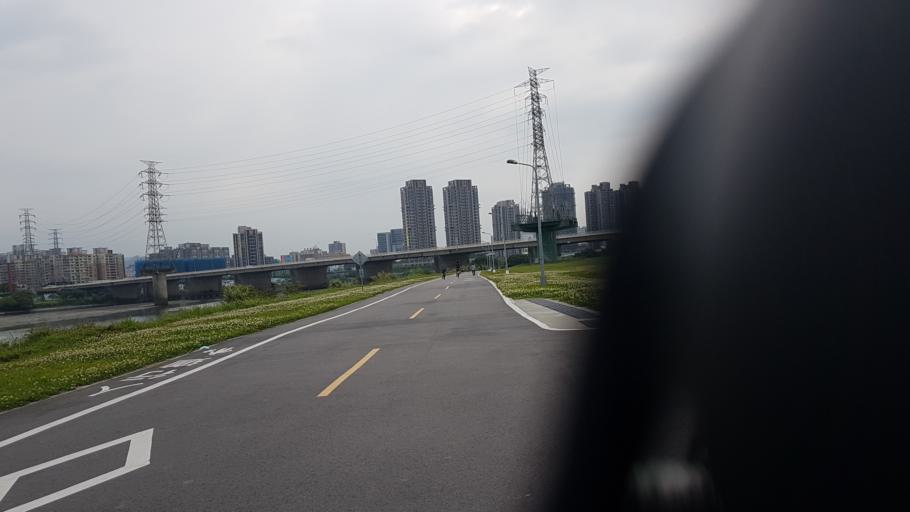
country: TW
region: Taipei
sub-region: Taipei
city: Banqiao
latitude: 25.0130
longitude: 121.4981
